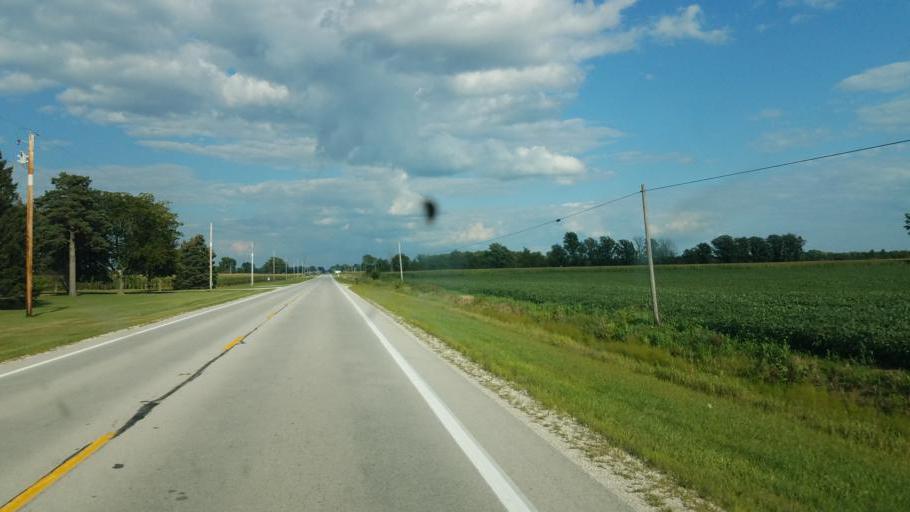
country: US
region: Ohio
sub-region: Sandusky County
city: Gibsonburg
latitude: 41.3413
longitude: -83.3981
